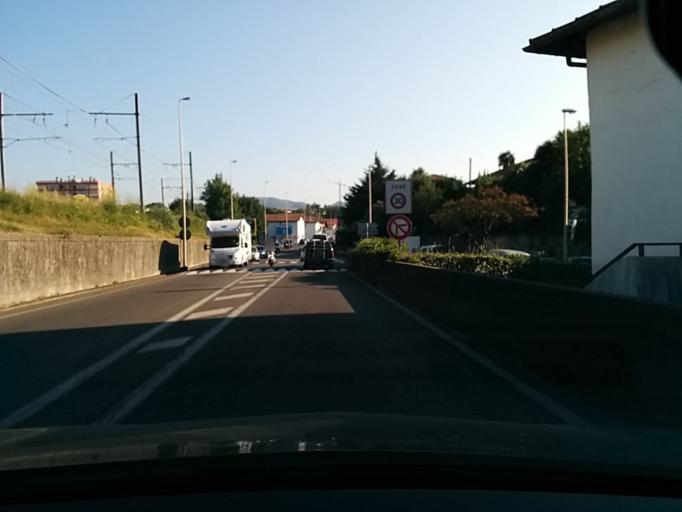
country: FR
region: Aquitaine
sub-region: Departement des Pyrenees-Atlantiques
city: Saint-Jean-de-Luz
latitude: 43.3824
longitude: -1.6673
